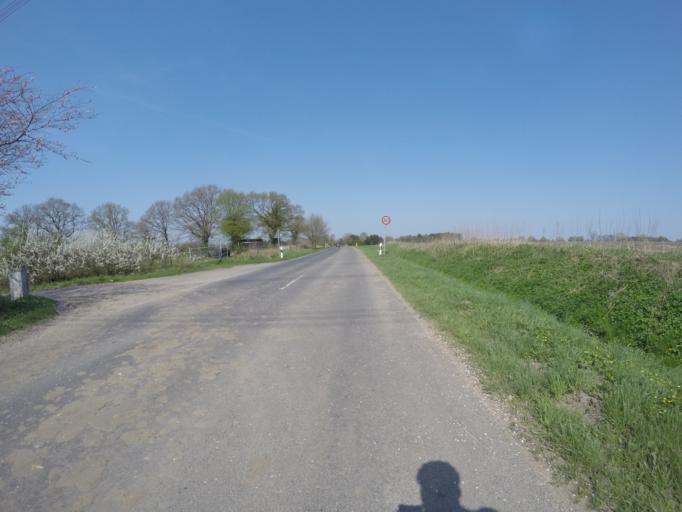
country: DE
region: Schleswig-Holstein
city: Quickborn
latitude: 53.7191
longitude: 9.8859
